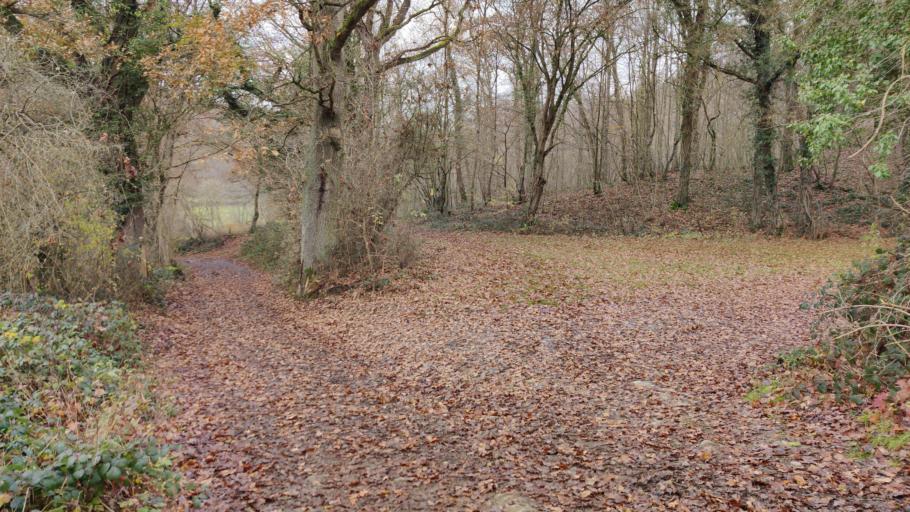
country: BE
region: Wallonia
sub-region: Province de Namur
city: Couvin
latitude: 50.0816
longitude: 4.5976
